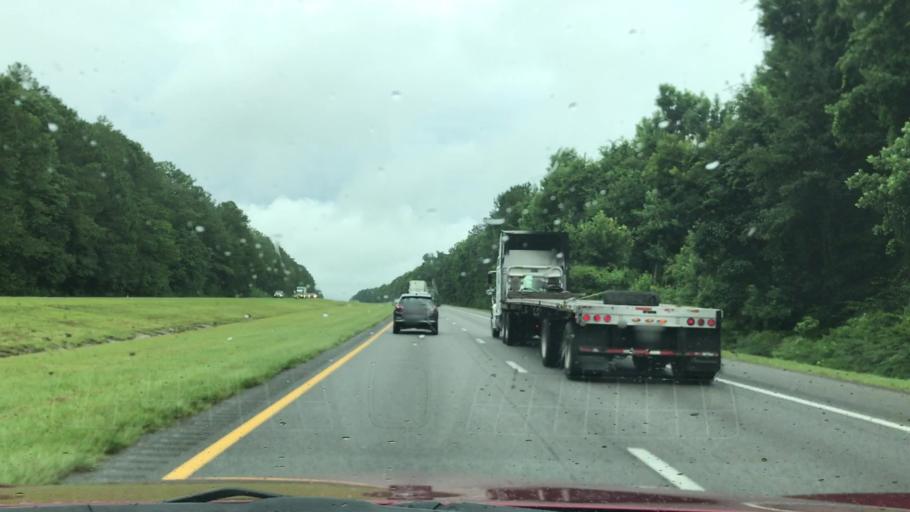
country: US
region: South Carolina
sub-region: Dorchester County
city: Ridgeville
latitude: 33.0947
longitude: -80.2331
